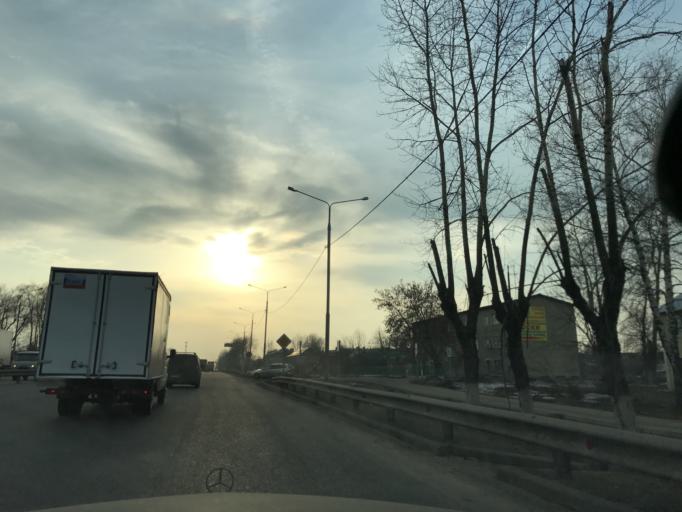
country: RU
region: Vladimir
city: Sobinka
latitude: 56.0259
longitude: 39.9949
